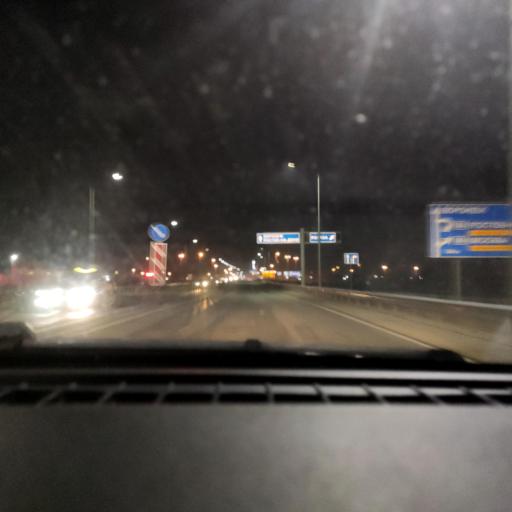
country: RU
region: Voronezj
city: Somovo
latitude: 51.6776
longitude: 39.3102
